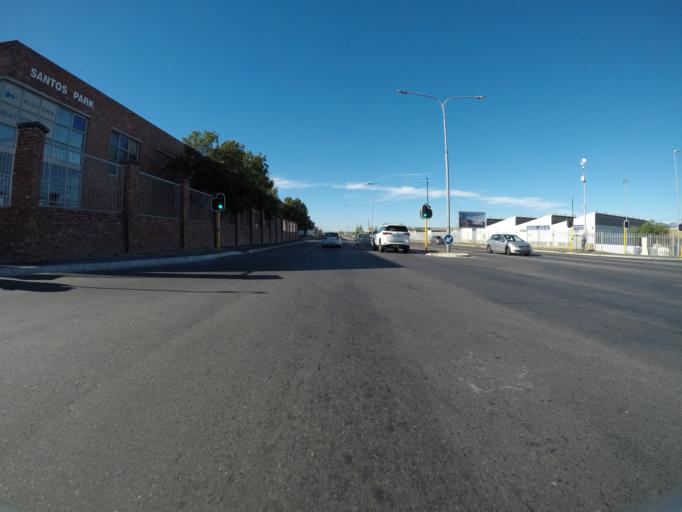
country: ZA
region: Western Cape
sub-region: City of Cape Town
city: Kraaifontein
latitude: -33.8994
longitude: 18.6703
